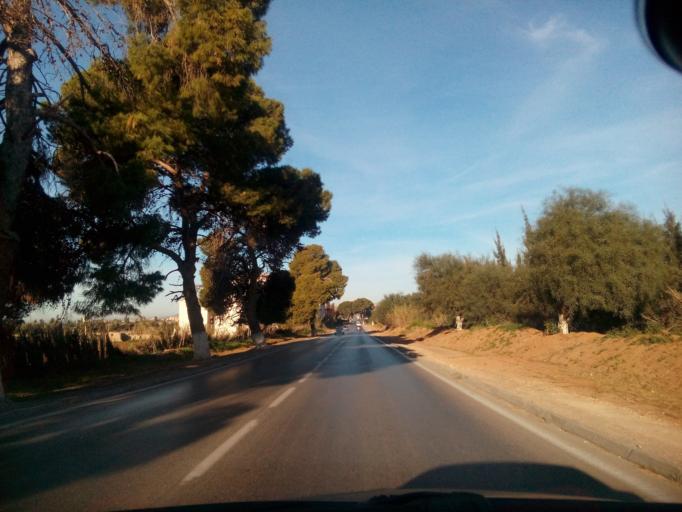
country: DZ
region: Mostaganem
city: Mostaganem
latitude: 35.7754
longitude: 0.1976
